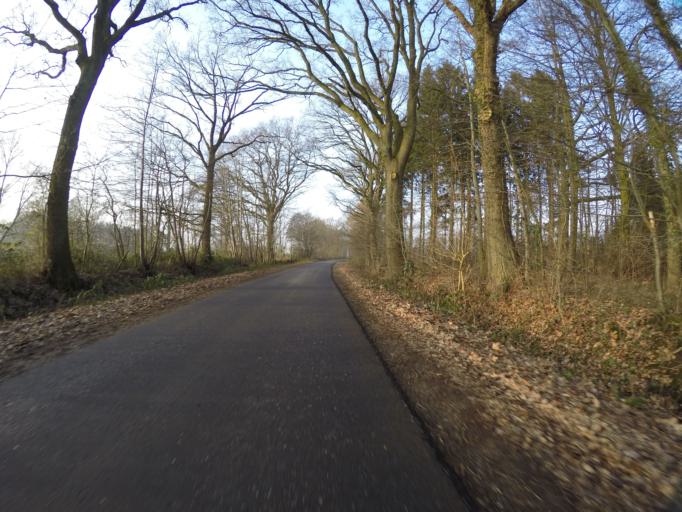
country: DE
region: Schleswig-Holstein
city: Hasloh
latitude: 53.6984
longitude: 9.8931
